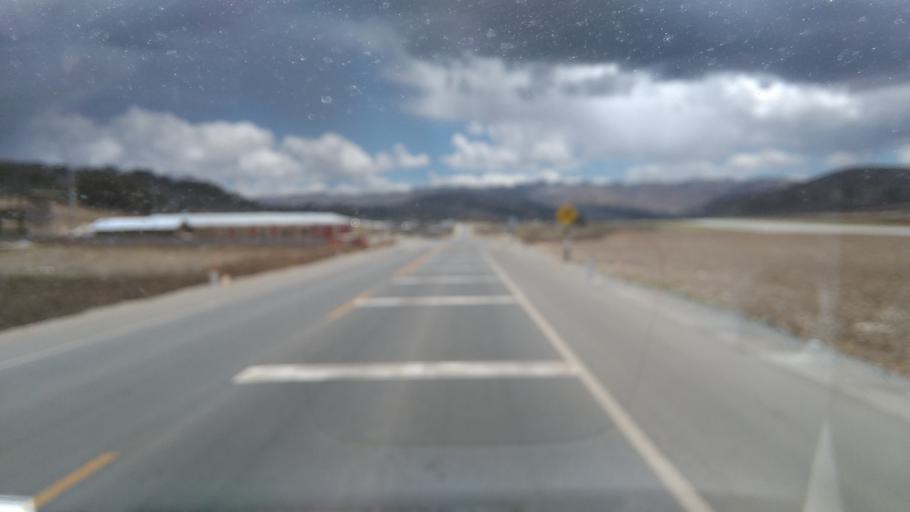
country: PE
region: Apurimac
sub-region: Provincia de Andahuaylas
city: San Jeronimo
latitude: -13.7050
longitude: -73.3488
